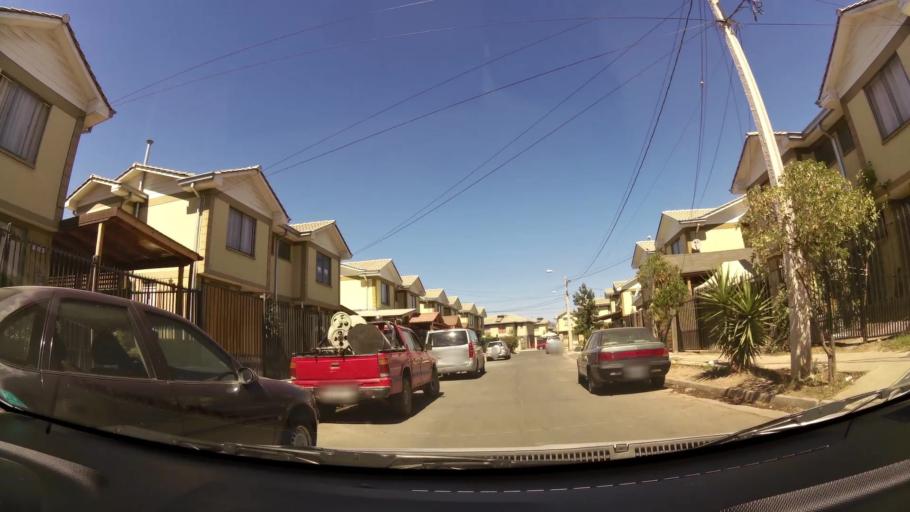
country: CL
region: O'Higgins
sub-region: Provincia de Cachapoal
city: Rancagua
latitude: -34.1749
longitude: -70.7703
